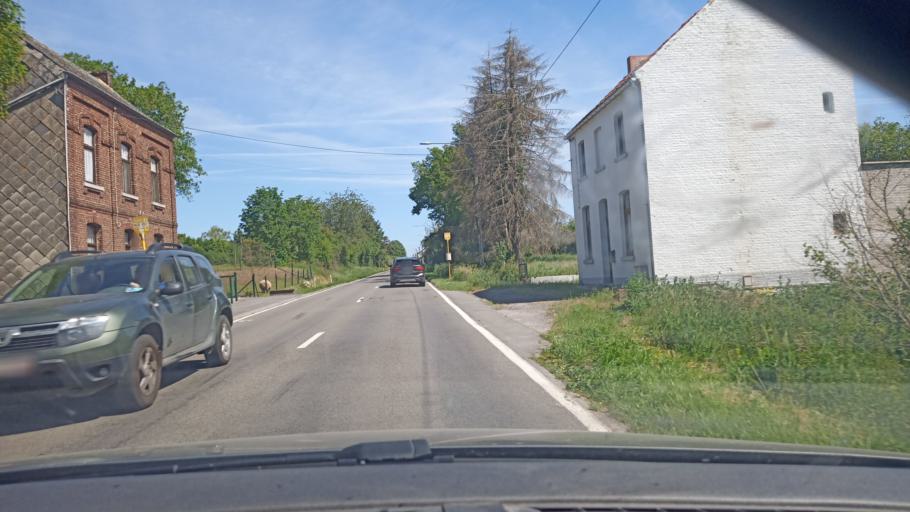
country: BE
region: Wallonia
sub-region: Province du Hainaut
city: Lobbes
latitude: 50.3319
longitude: 4.2637
